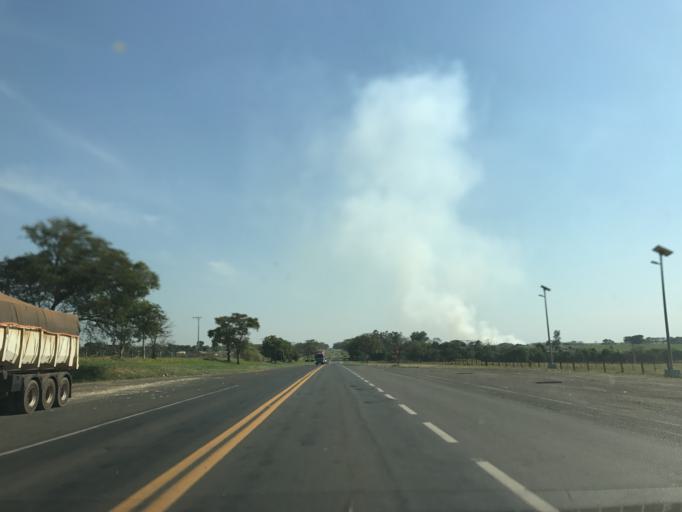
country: BR
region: Sao Paulo
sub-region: Penapolis
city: Penapolis
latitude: -21.3806
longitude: -50.0897
